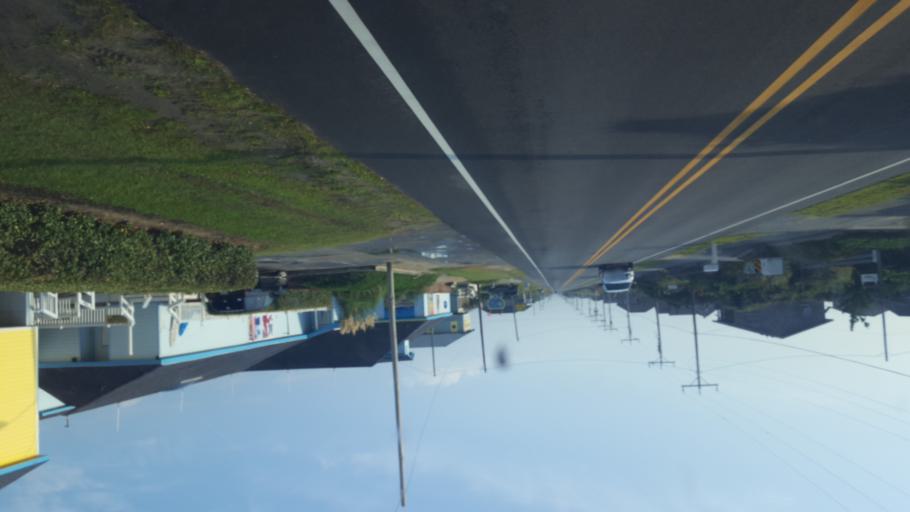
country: US
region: North Carolina
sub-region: Dare County
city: Nags Head
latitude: 35.9587
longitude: -75.6249
